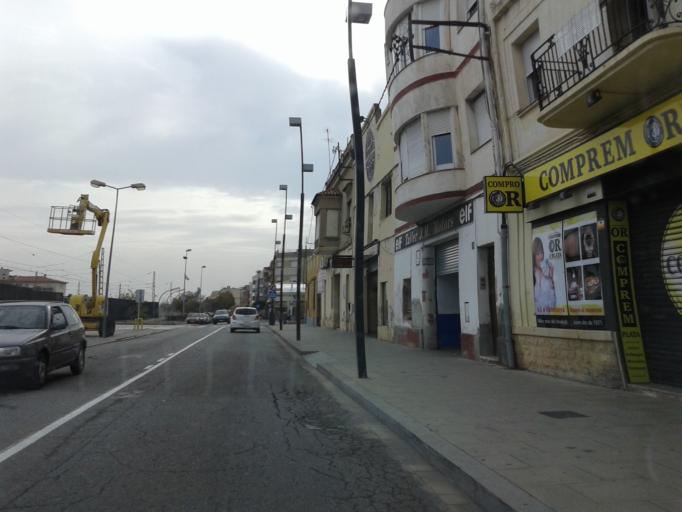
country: ES
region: Catalonia
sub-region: Provincia de Tarragona
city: El Vendrell
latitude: 41.2204
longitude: 1.5373
